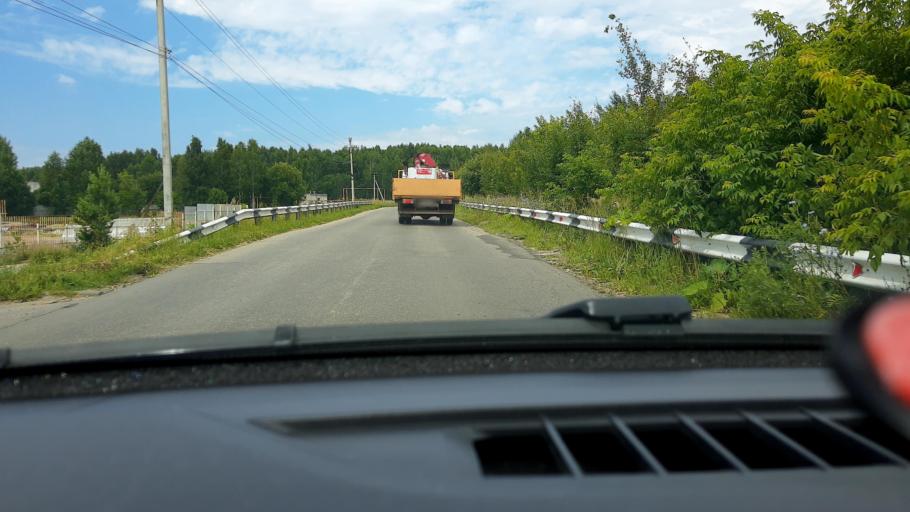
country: RU
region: Nizjnij Novgorod
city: Bogorodsk
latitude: 56.1387
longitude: 43.5888
